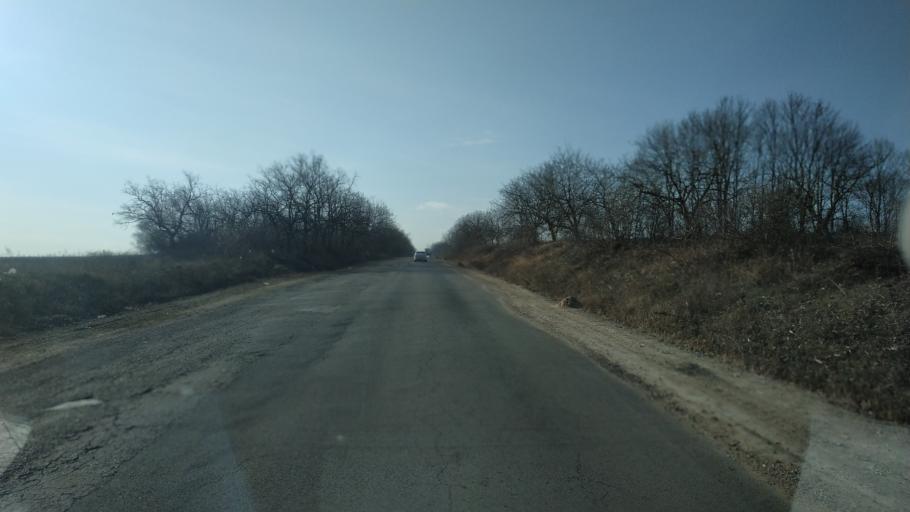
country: MD
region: Chisinau
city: Singera
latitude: 46.8731
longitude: 29.0397
